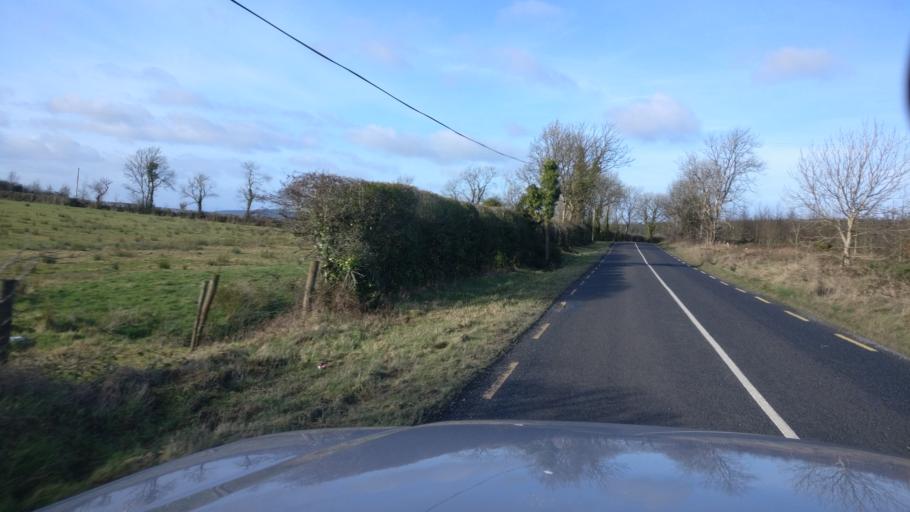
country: IE
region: Leinster
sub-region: Laois
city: Stradbally
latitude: 52.9164
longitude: -7.1868
